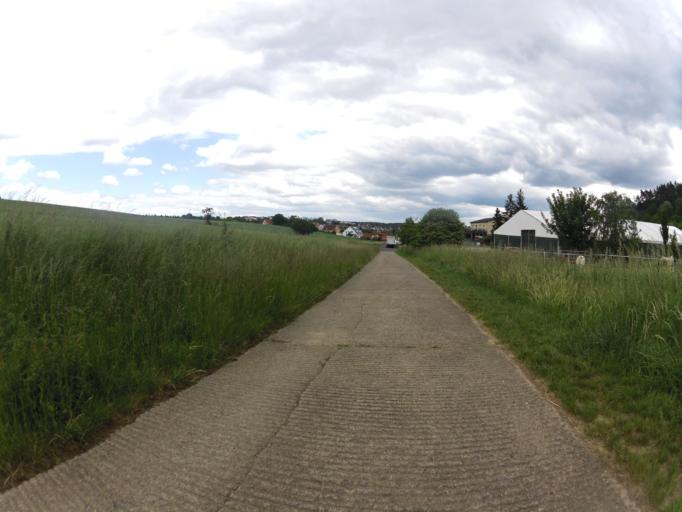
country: DE
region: Bavaria
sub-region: Regierungsbezirk Unterfranken
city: Guntersleben
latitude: 49.8738
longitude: 9.8881
